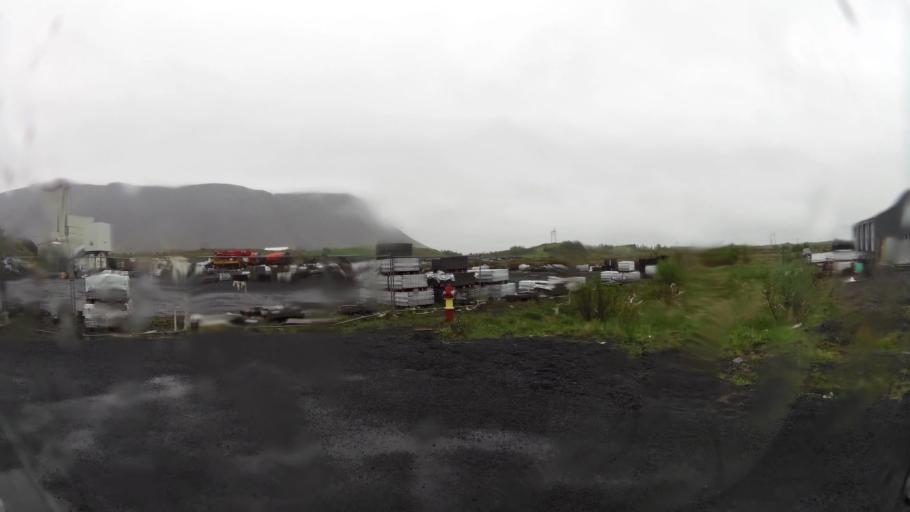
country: IS
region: South
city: Selfoss
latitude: 63.9484
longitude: -21.0091
